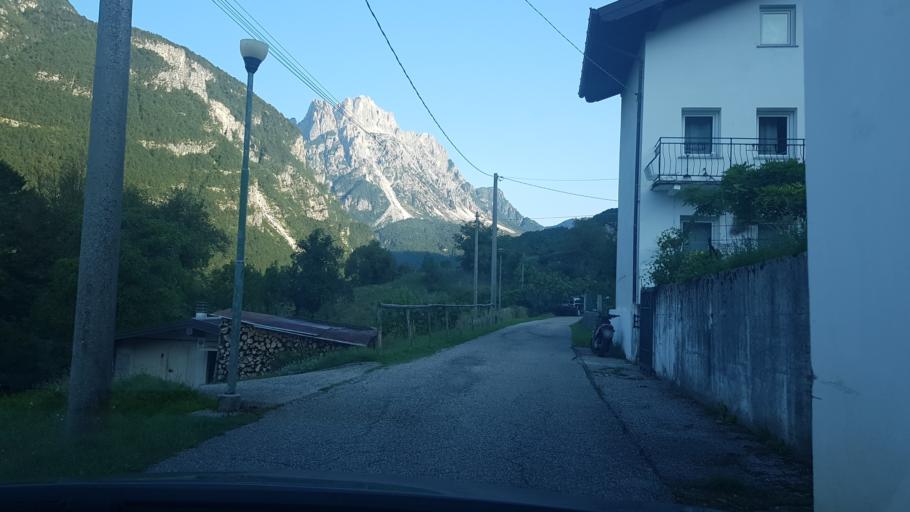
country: IT
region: Friuli Venezia Giulia
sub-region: Provincia di Udine
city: Moggio Udinese
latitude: 46.4285
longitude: 13.2055
